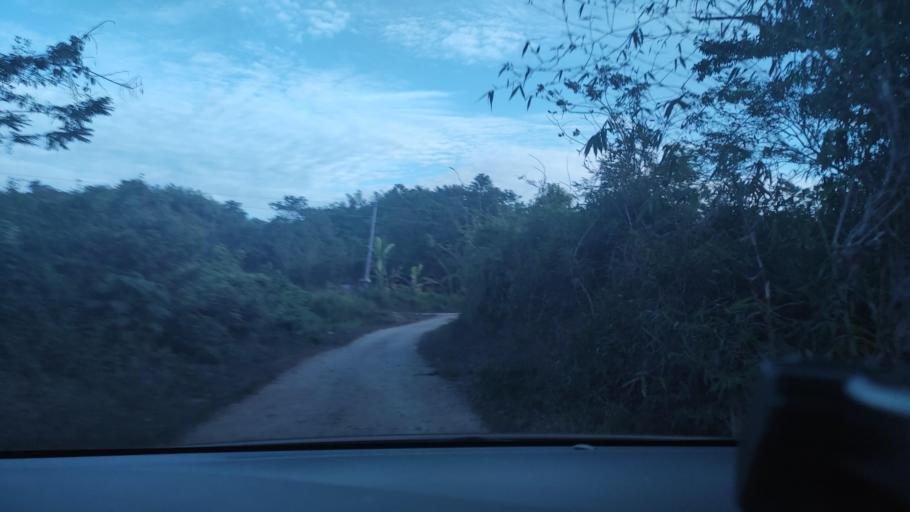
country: PH
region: Ilocos
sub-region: Province of Pangasinan
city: Balingasay
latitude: 16.3059
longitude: 119.8599
